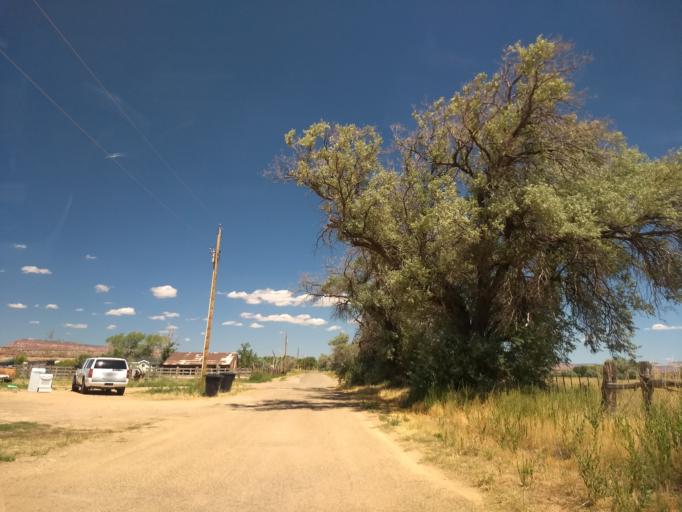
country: US
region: Arizona
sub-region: Coconino County
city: Fredonia
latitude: 36.9322
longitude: -112.5353
